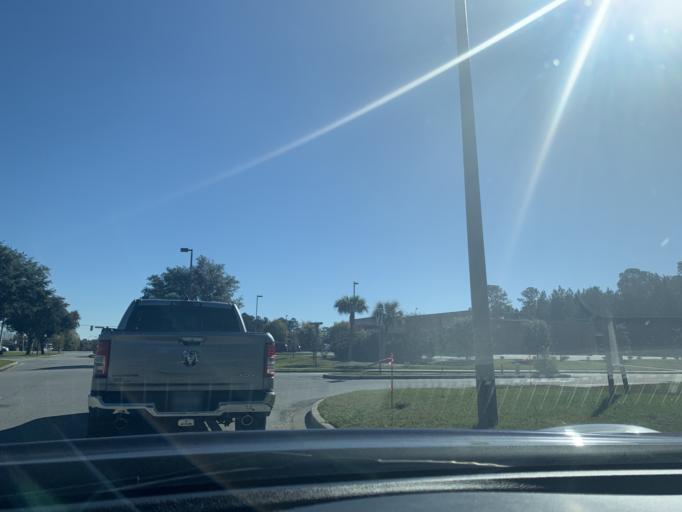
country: US
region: Georgia
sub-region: Chatham County
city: Pooler
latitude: 32.1360
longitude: -81.2561
